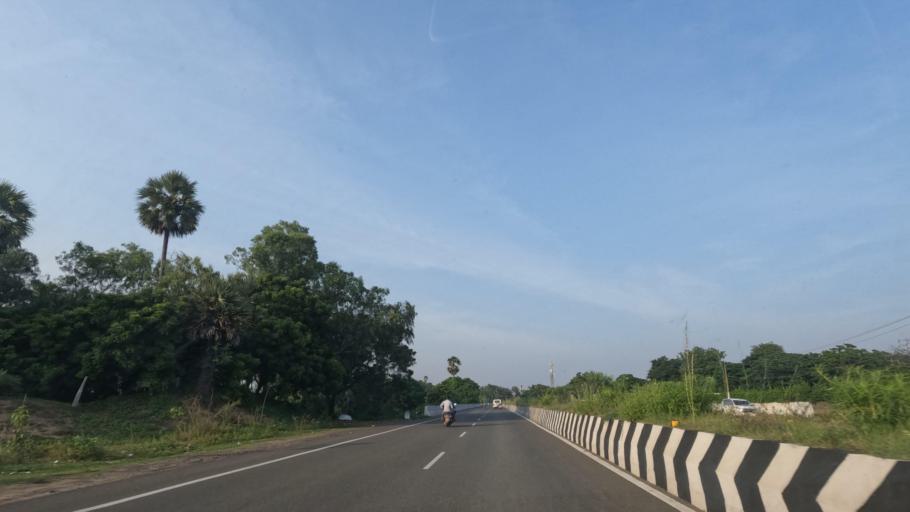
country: IN
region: Tamil Nadu
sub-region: Kancheepuram
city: Mamallapuram
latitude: 12.6490
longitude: 80.2035
